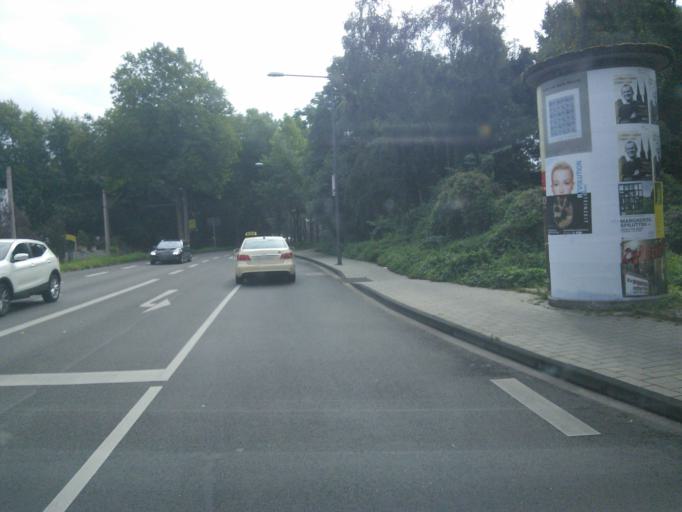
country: DE
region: North Rhine-Westphalia
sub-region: Regierungsbezirk Koln
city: Mengenich
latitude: 50.9663
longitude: 6.8814
